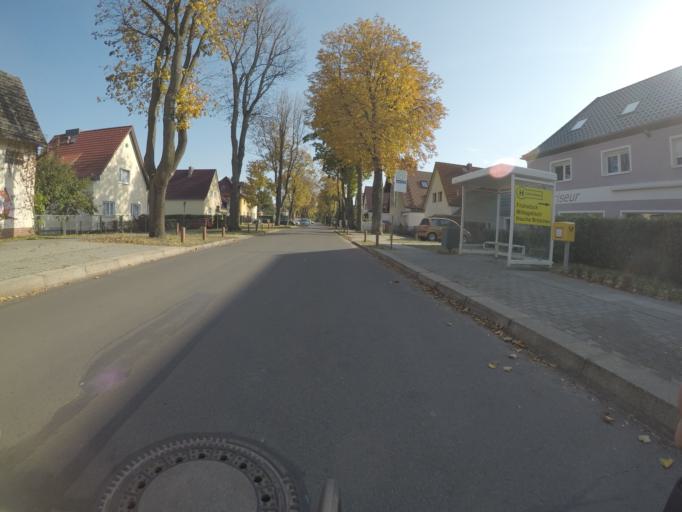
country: DE
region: Brandenburg
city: Hohen Neuendorf
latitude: 52.6795
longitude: 13.2511
